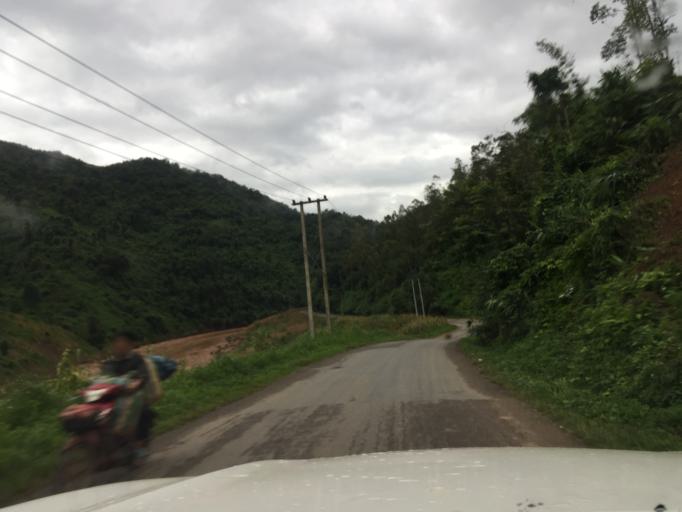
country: LA
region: Oudomxai
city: Muang La
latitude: 20.9539
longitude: 102.2151
